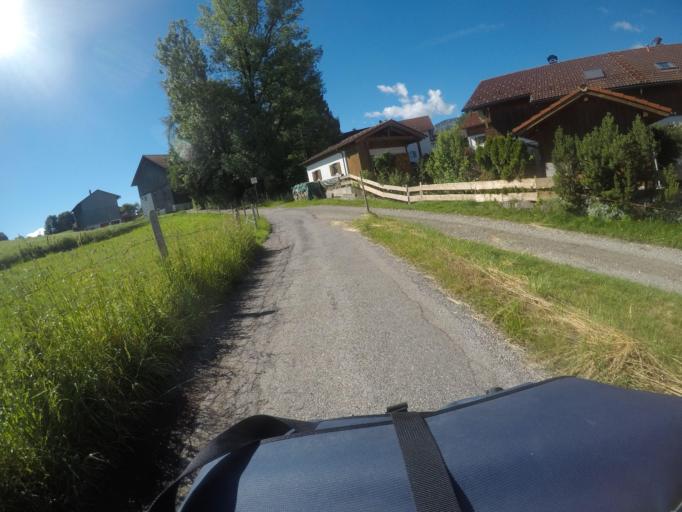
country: DE
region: Bavaria
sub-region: Swabia
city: Pfronten
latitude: 47.5981
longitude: 10.5672
